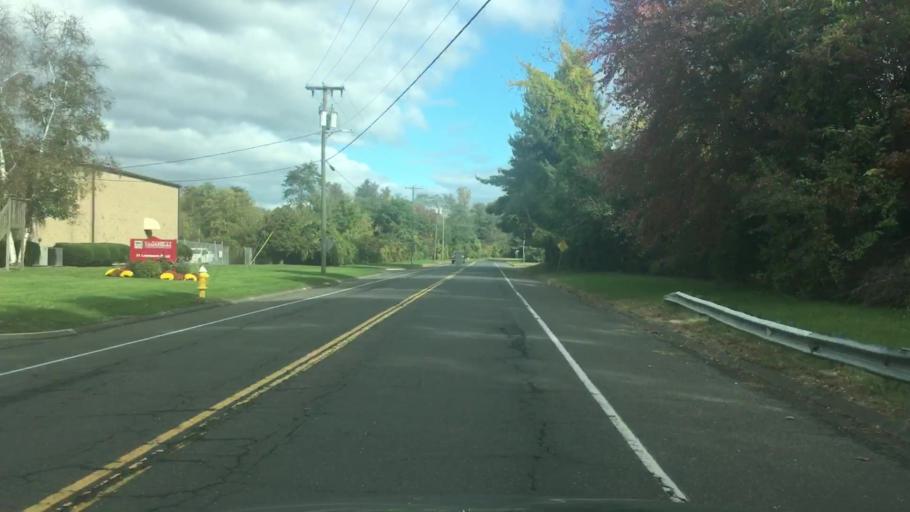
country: US
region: Connecticut
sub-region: Hartford County
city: Windsor Locks
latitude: 41.9068
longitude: -72.6314
